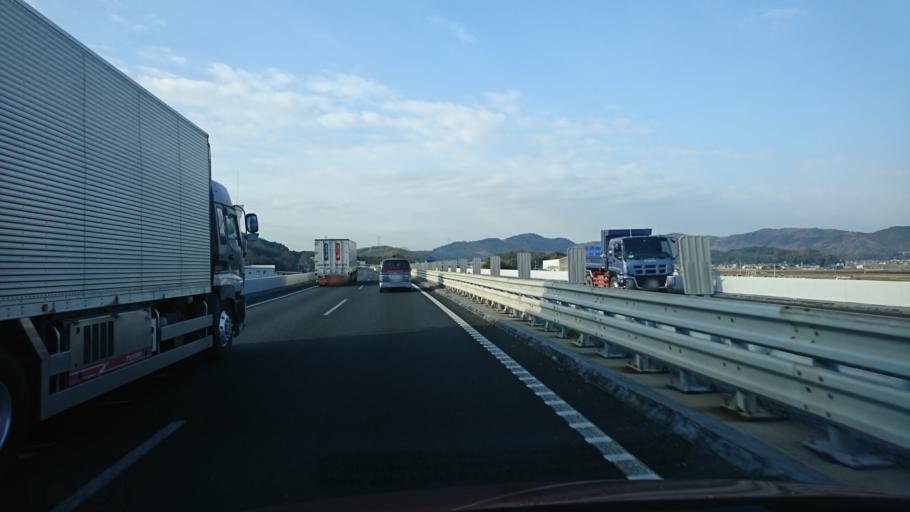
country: JP
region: Hyogo
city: Tatsunocho-tominaga
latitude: 34.8450
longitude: 134.5196
